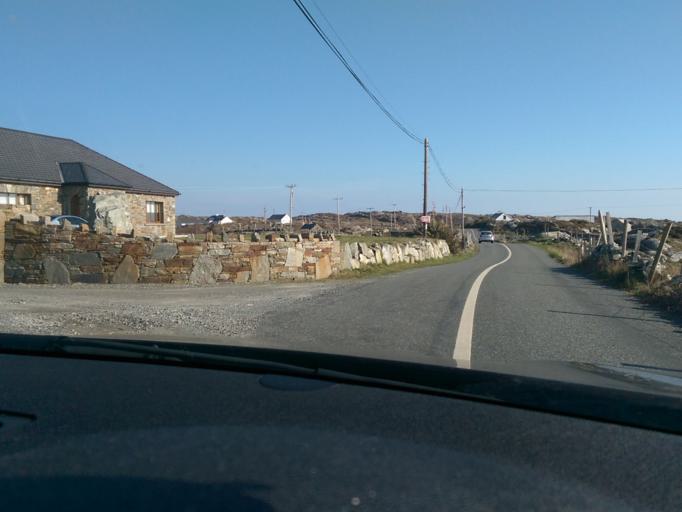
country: IE
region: Connaught
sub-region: County Galway
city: Clifden
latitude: 53.3984
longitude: -10.0291
